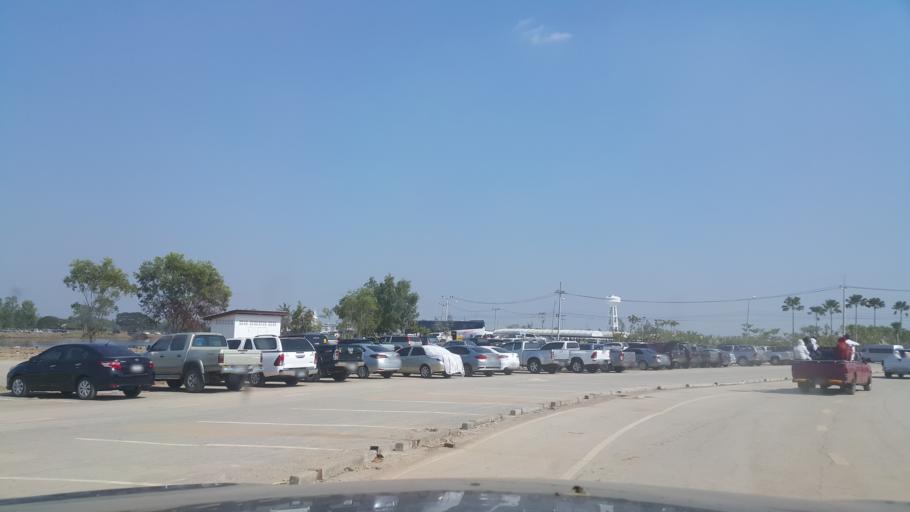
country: TH
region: Khon Kaen
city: Khon Kaen
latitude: 16.5134
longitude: 102.8681
